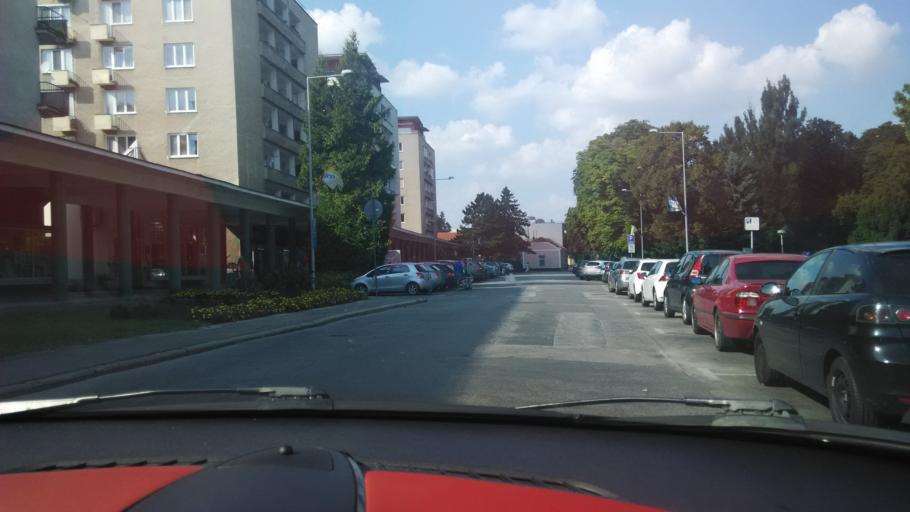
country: SK
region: Trnavsky
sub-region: Okres Trnava
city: Piestany
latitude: 48.5910
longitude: 17.8349
